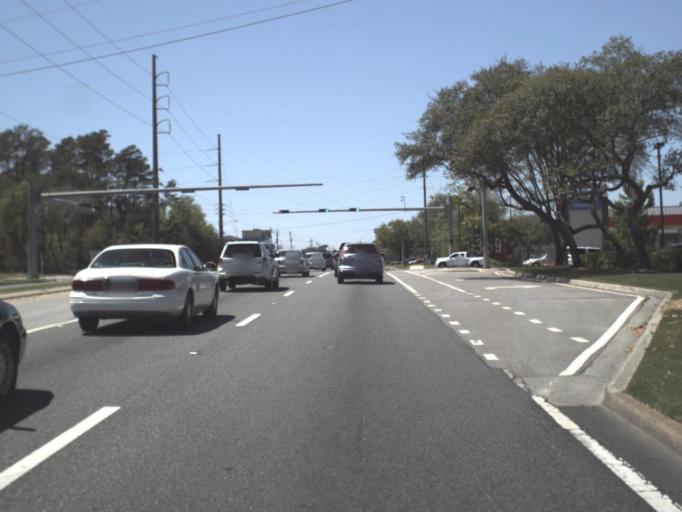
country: US
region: Florida
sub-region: Okaloosa County
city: Niceville
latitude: 30.5151
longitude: -86.4617
